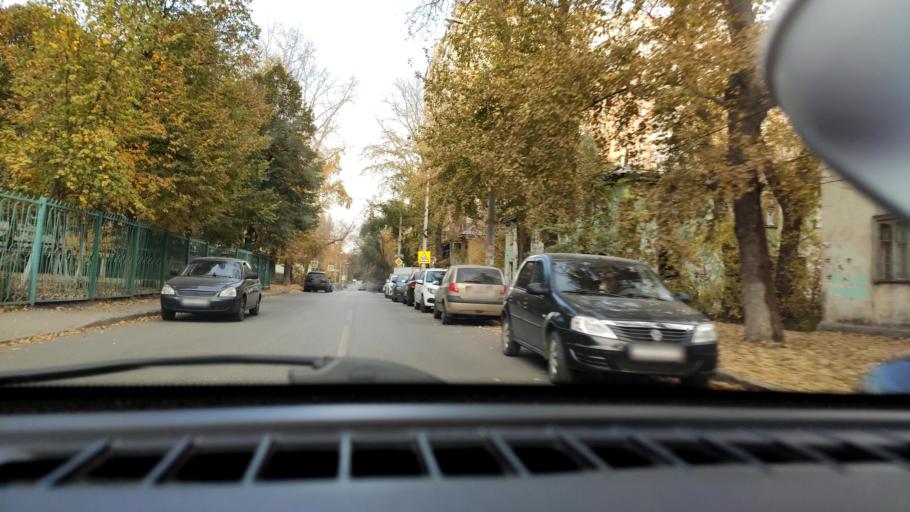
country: RU
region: Samara
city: Samara
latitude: 53.2285
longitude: 50.2590
